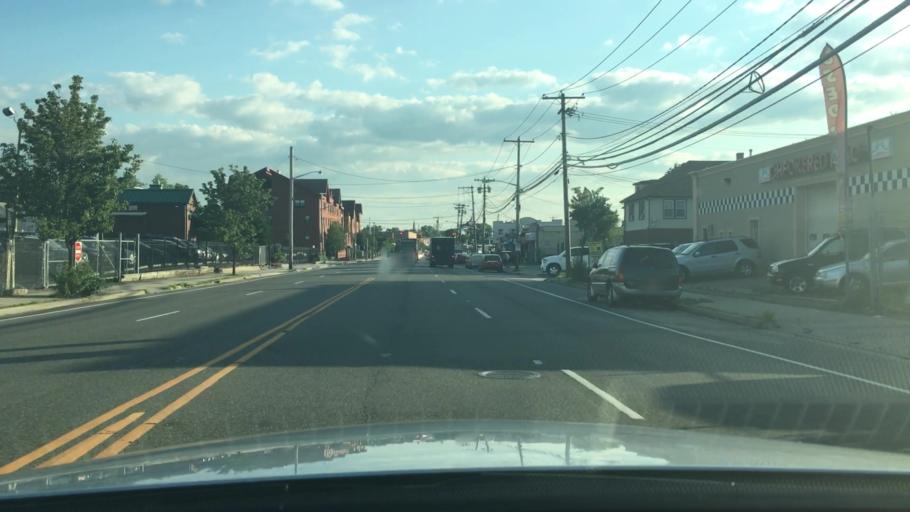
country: US
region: New York
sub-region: Nassau County
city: Westbury
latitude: 40.7580
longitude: -73.5792
